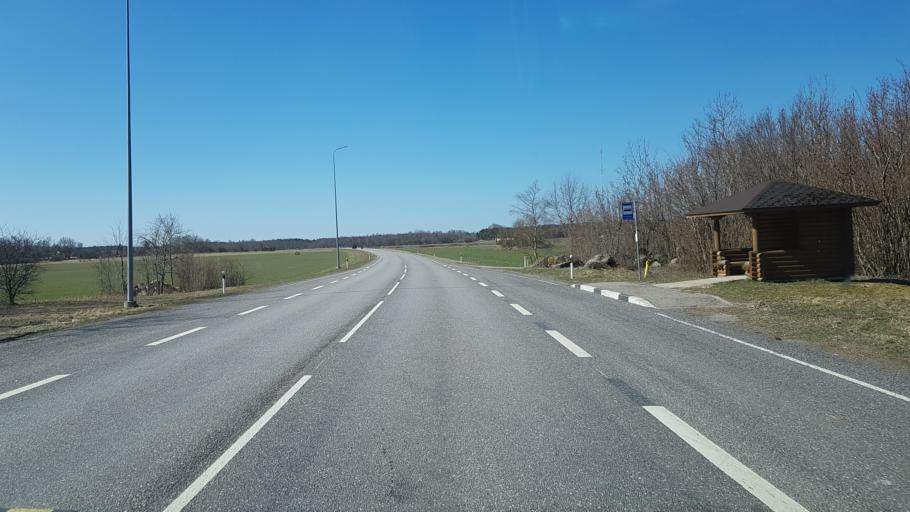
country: EE
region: Saare
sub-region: Orissaare vald
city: Orissaare
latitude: 58.5182
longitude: 22.8894
